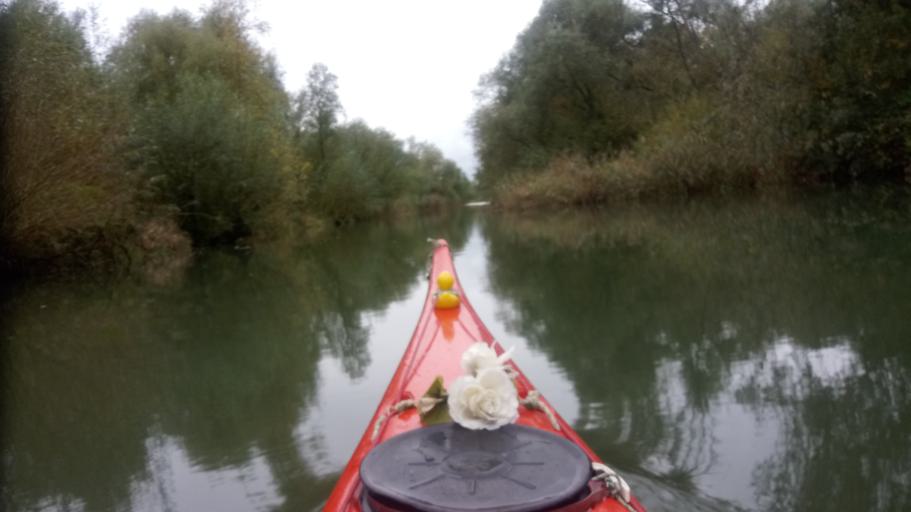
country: NL
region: North Brabant
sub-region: Gemeente Made en Drimmelen
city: Drimmelen
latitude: 51.7552
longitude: 4.7638
